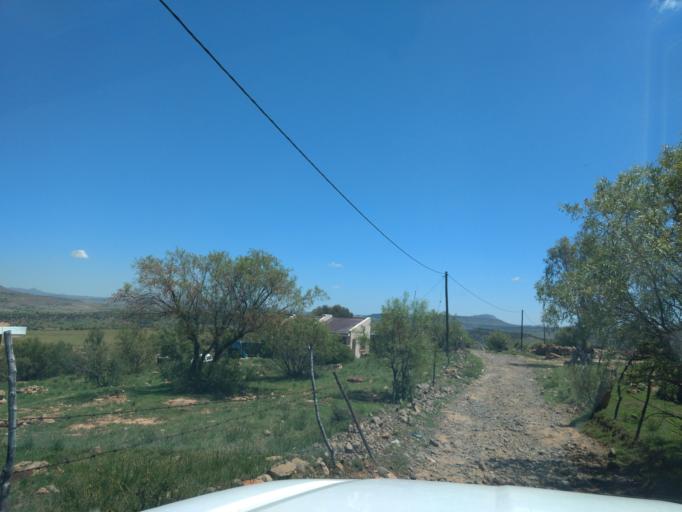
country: LS
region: Maseru
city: Maseru
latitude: -29.4579
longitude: 27.3724
